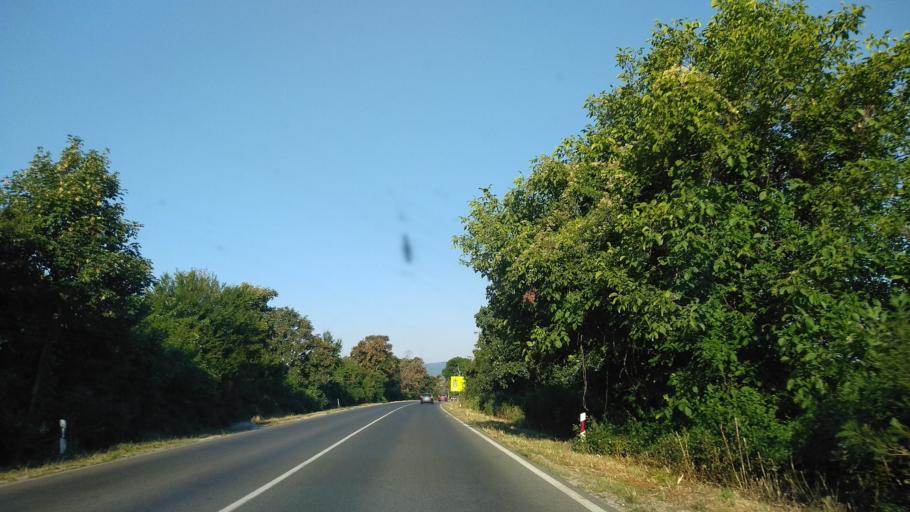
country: BG
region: Gabrovo
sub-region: Obshtina Sevlievo
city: Sevlievo
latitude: 43.0358
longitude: 25.1422
